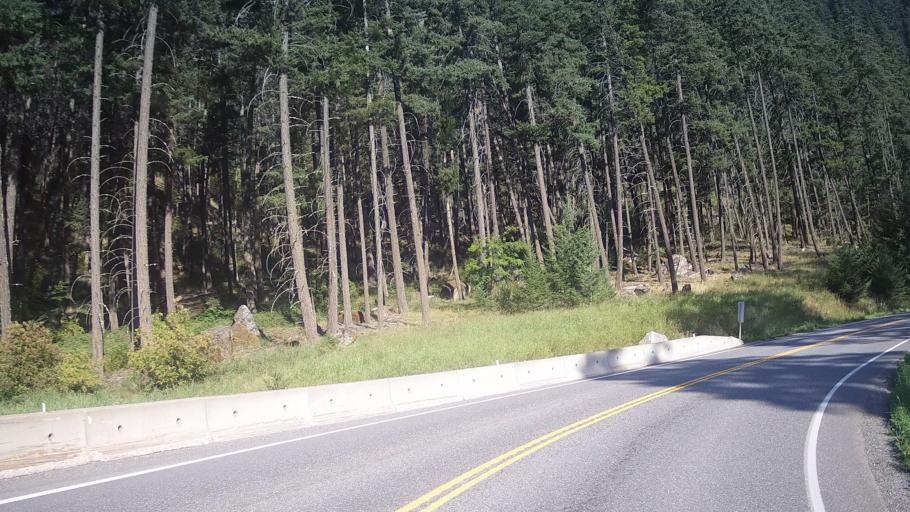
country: CA
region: British Columbia
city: Lillooet
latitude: 50.6524
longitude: -122.0103
